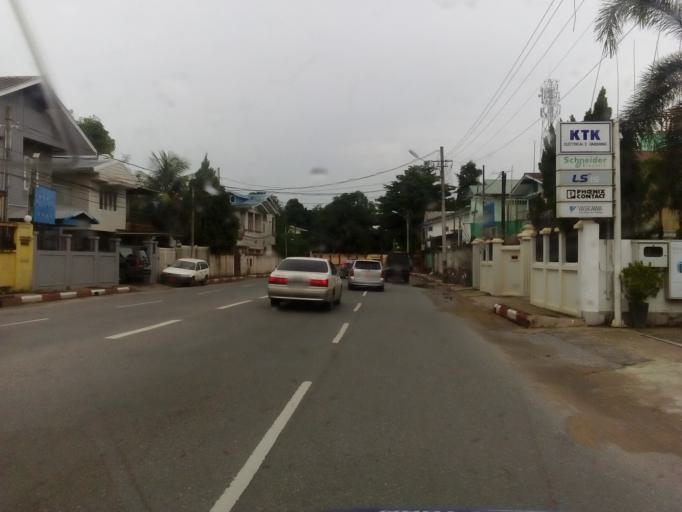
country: MM
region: Yangon
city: Yangon
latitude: 16.8522
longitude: 96.1493
